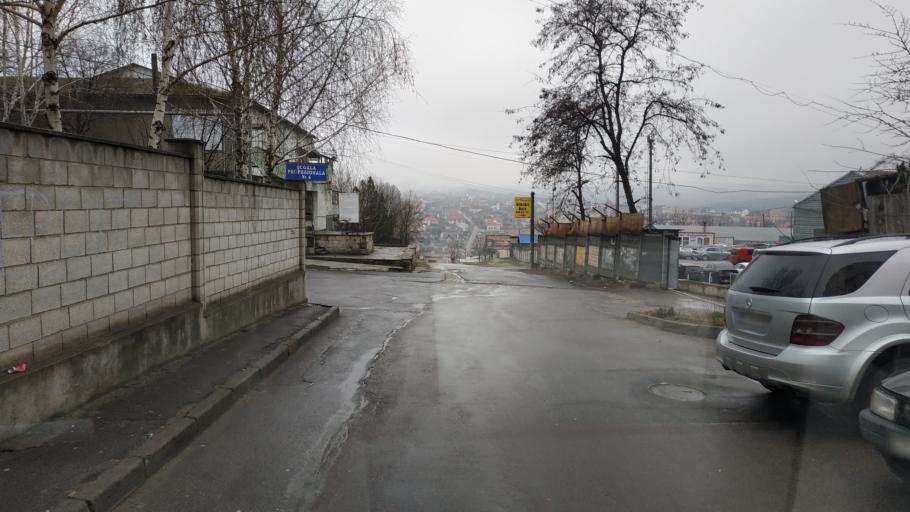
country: MD
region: Chisinau
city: Vatra
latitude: 47.0363
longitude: 28.7675
